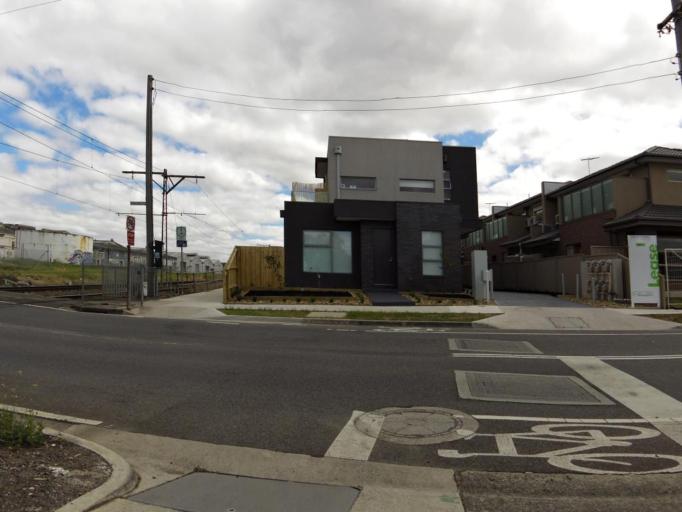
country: AU
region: Victoria
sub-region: Moreland
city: Coburg North
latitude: -37.7274
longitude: 144.9622
